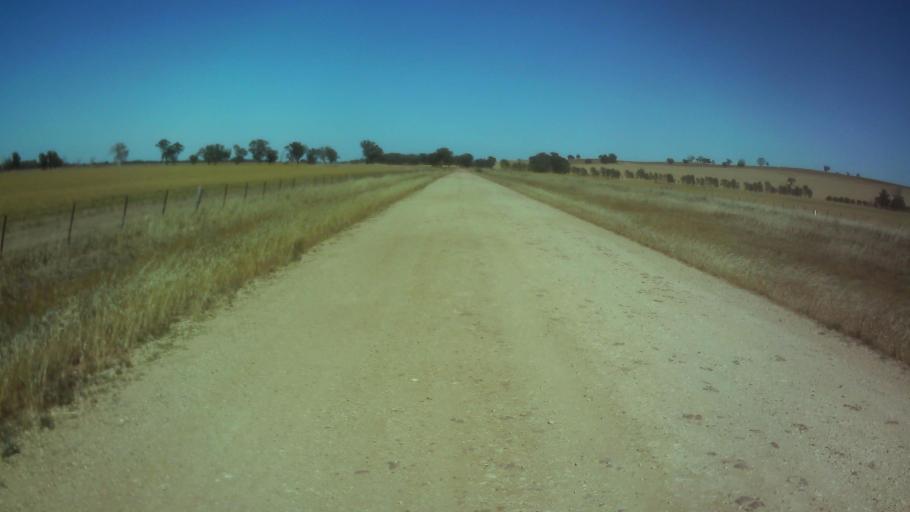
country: AU
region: New South Wales
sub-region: Weddin
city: Grenfell
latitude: -33.9954
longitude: 148.3650
